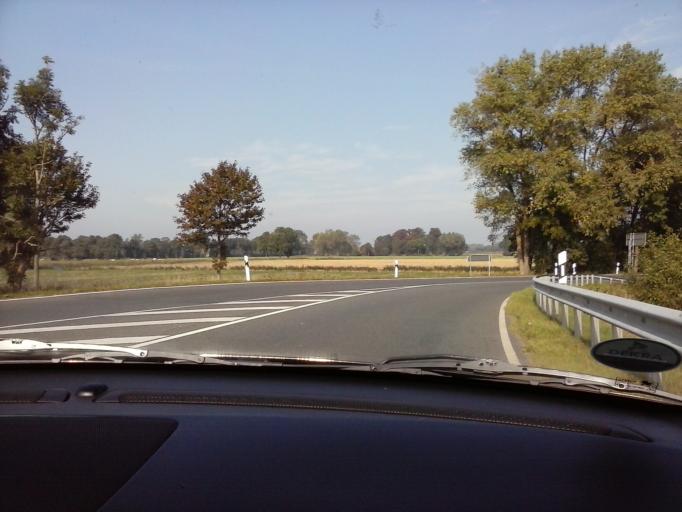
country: DE
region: Lower Saxony
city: Otterndorf
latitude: 53.8000
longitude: 8.8674
